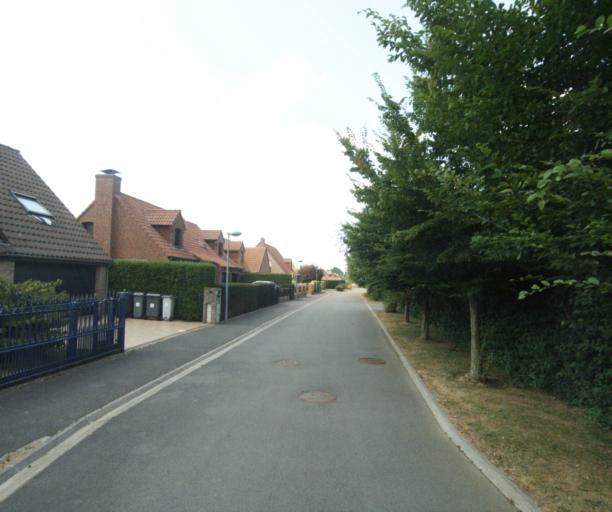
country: FR
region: Nord-Pas-de-Calais
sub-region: Departement du Nord
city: Comines
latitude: 50.7384
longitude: 3.0170
